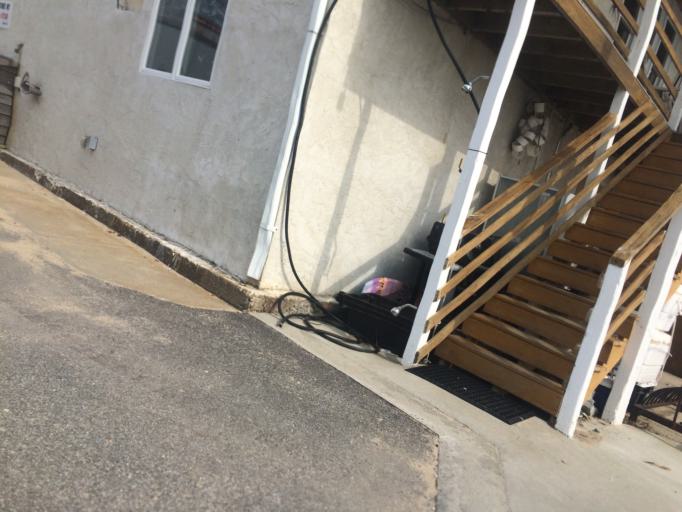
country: US
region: Massachusetts
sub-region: Barnstable County
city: Provincetown
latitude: 42.0454
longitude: -70.1911
